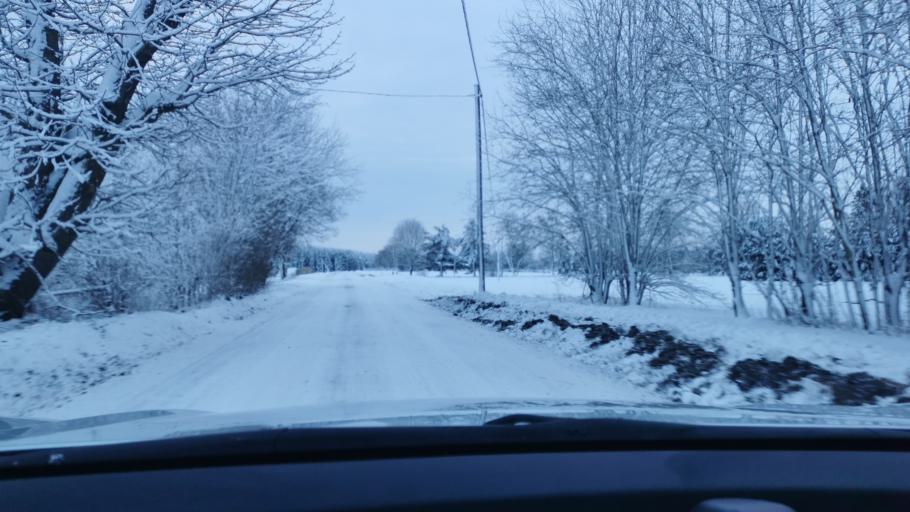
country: EE
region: Laeaene-Virumaa
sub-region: Viru-Nigula vald
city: Kunda
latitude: 59.4210
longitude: 26.5203
